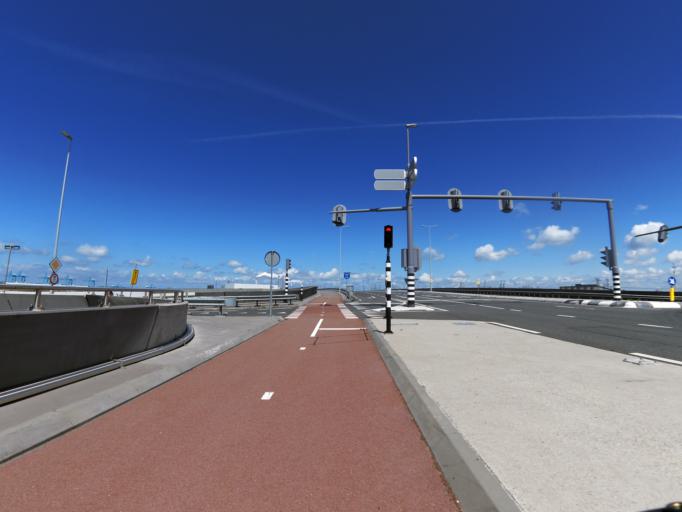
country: NL
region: South Holland
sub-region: Gemeente Goeree-Overflakkee
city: Goedereede
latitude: 51.9325
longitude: 4.0190
